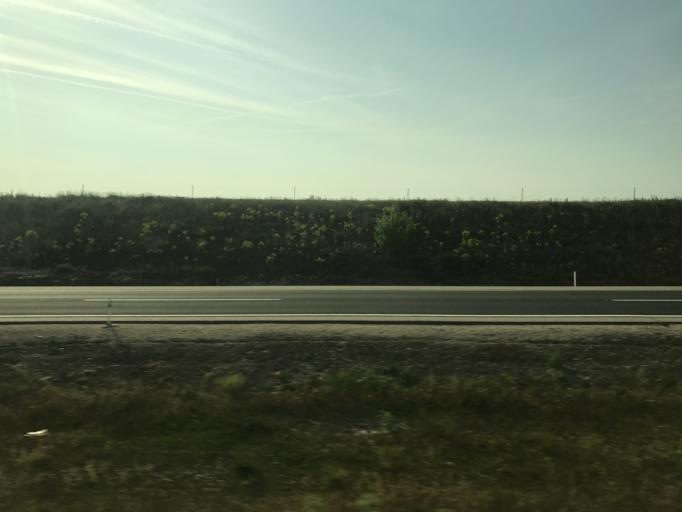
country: ES
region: Castille and Leon
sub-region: Provincia de Burgos
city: Zuneda
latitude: 42.5962
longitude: -3.2273
